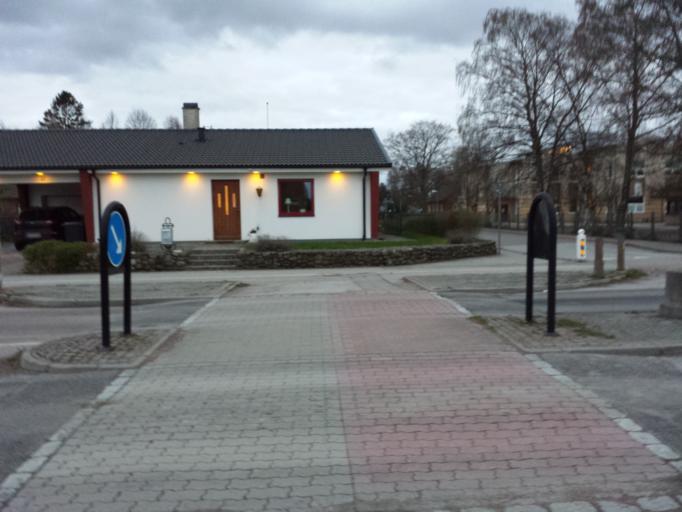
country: SE
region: Skane
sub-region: Sjobo Kommun
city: Sjoebo
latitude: 55.6337
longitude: 13.6963
